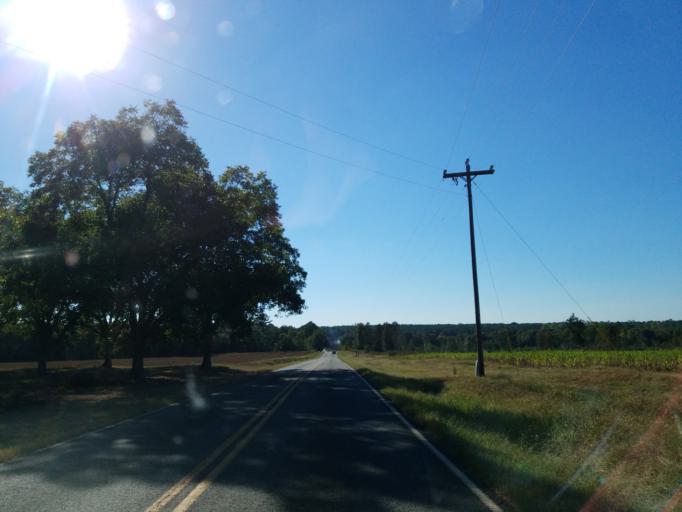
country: US
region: Georgia
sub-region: Dooly County
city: Unadilla
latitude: 32.2446
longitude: -83.8293
